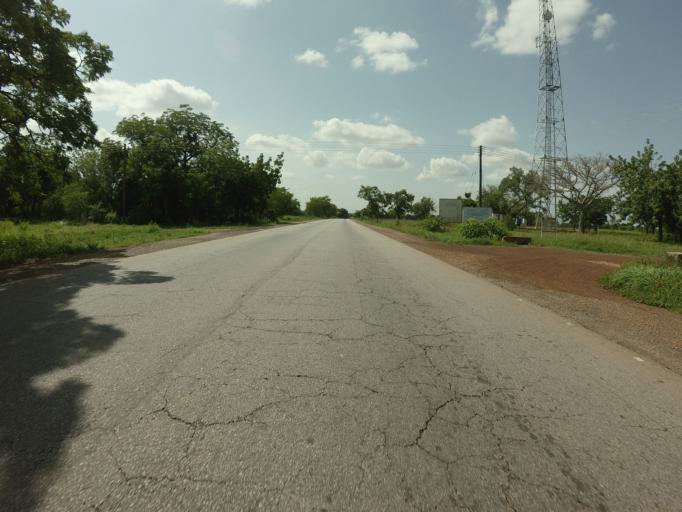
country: GH
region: Northern
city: Savelugu
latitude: 9.8176
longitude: -0.8626
